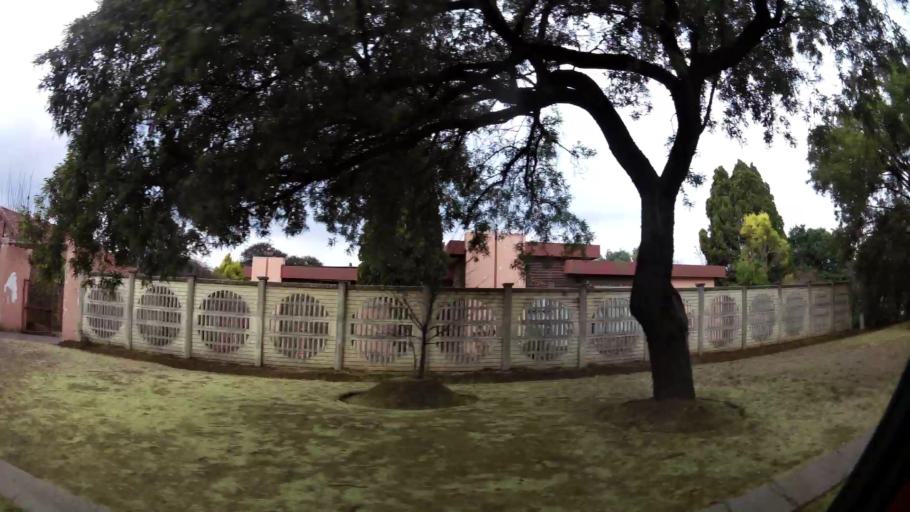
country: ZA
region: Gauteng
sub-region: Sedibeng District Municipality
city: Vanderbijlpark
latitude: -26.7052
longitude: 27.7953
